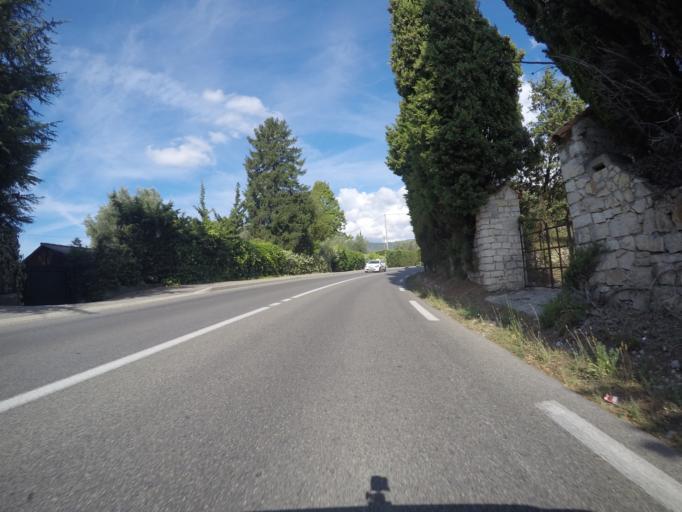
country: FR
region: Provence-Alpes-Cote d'Azur
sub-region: Departement des Alpes-Maritimes
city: Opio
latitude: 43.6754
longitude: 6.9852
